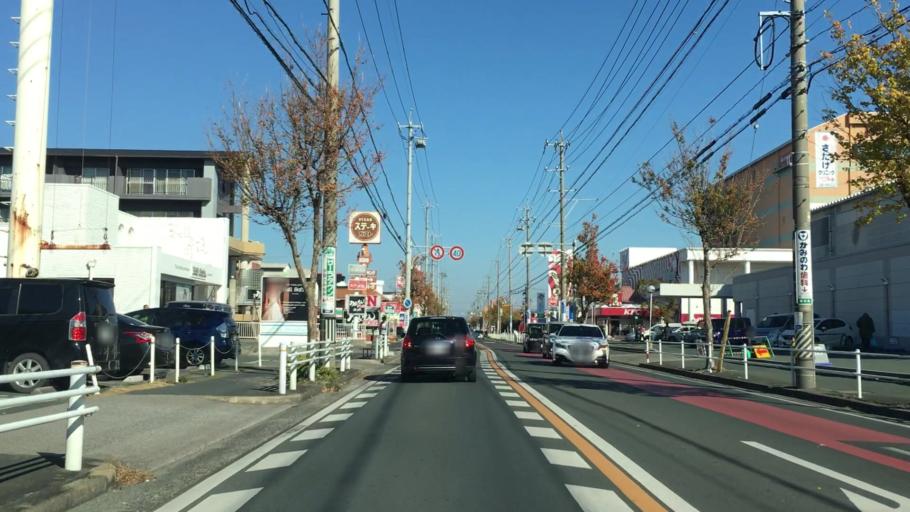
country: JP
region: Aichi
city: Toyohashi
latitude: 34.7437
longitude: 137.3699
